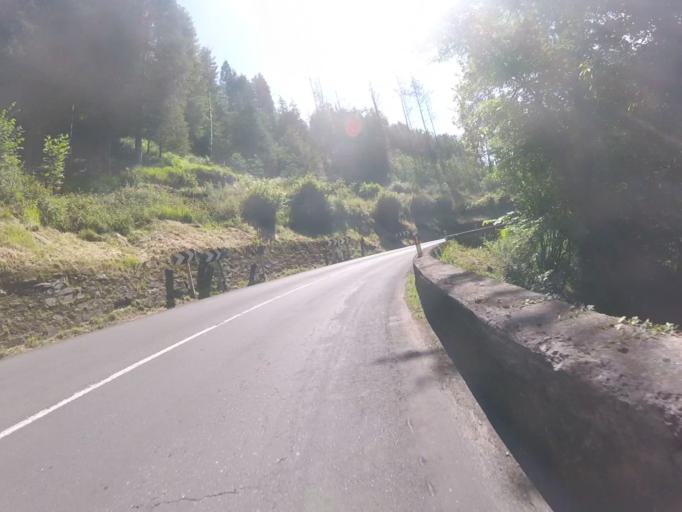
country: ES
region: Basque Country
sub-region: Provincia de Guipuzcoa
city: Errezil
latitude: 43.1752
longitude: -2.2142
